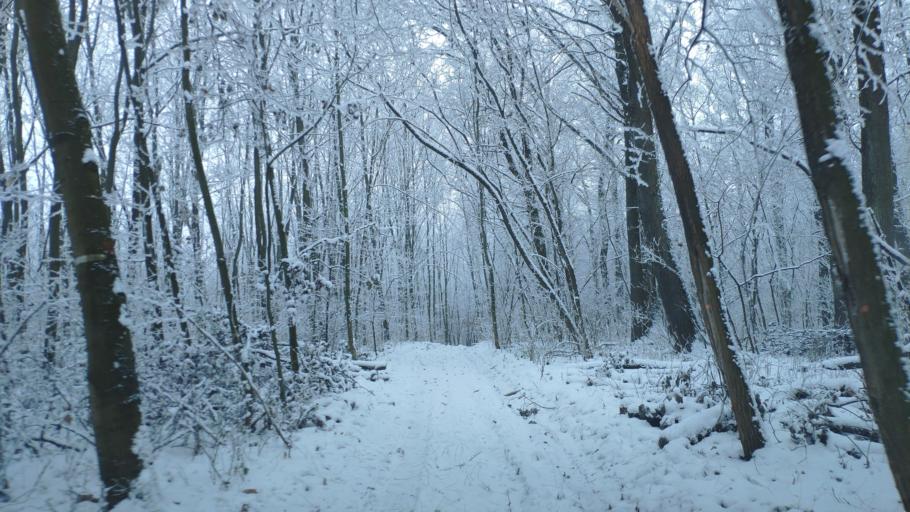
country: SK
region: Kosicky
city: Kosice
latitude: 48.6444
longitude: 21.1862
